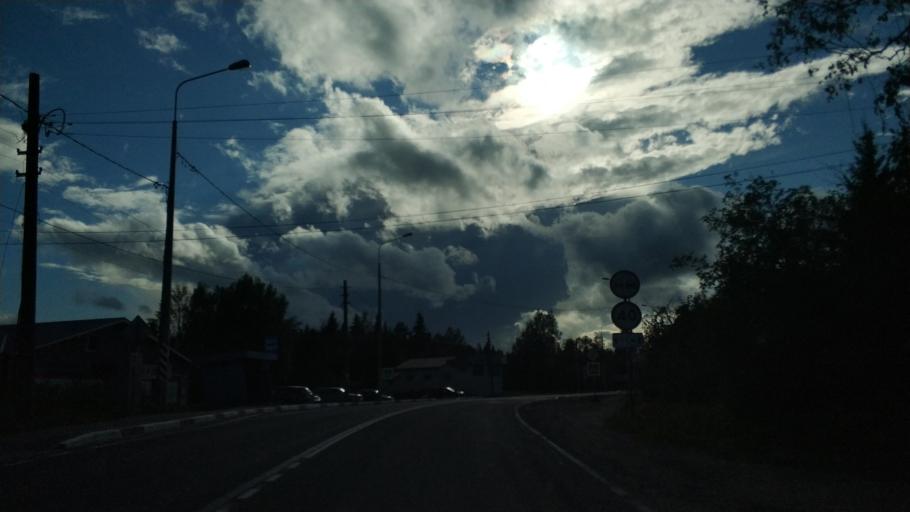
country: RU
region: Republic of Karelia
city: Lakhdenpokh'ya
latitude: 61.5179
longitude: 30.1531
